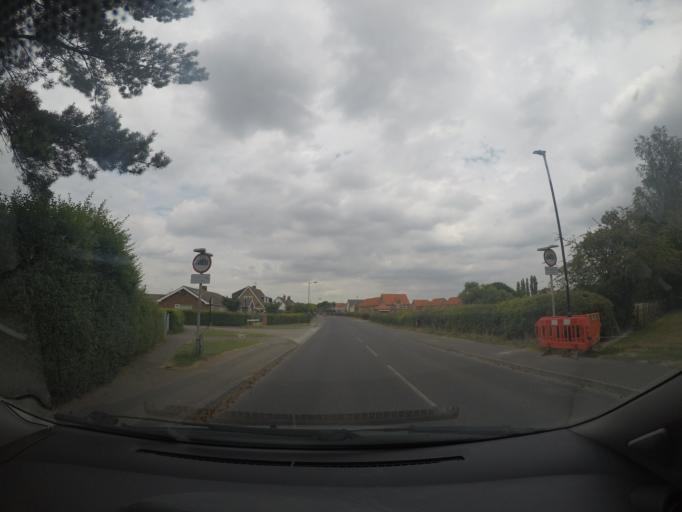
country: GB
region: England
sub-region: City of York
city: Huntington
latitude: 53.9898
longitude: -1.0591
